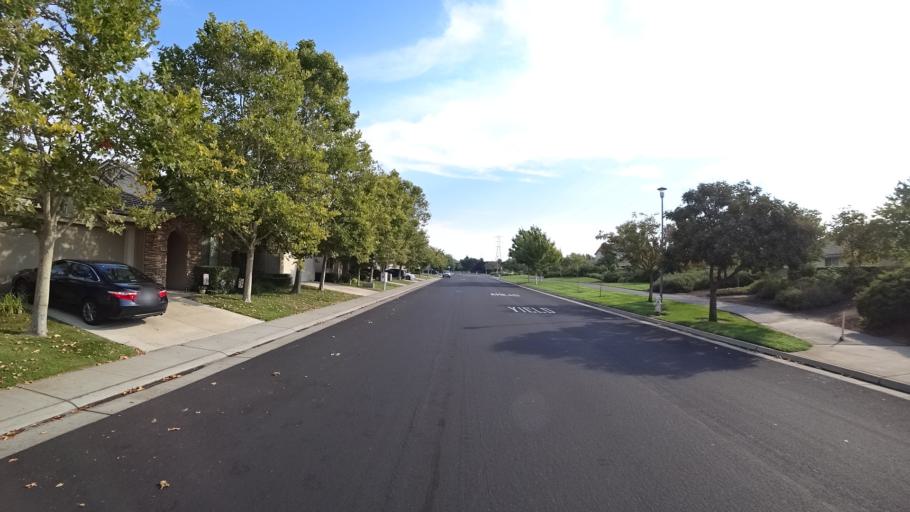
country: US
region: California
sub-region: Sacramento County
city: Laguna
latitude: 38.3993
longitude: -121.4677
